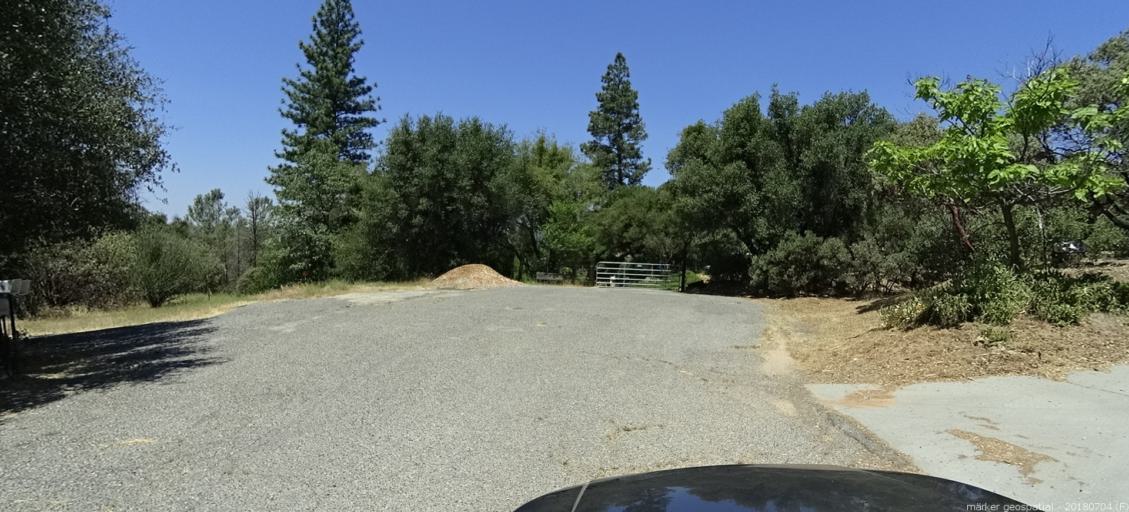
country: US
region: California
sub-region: Fresno County
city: Auberry
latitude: 37.2293
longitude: -119.4859
